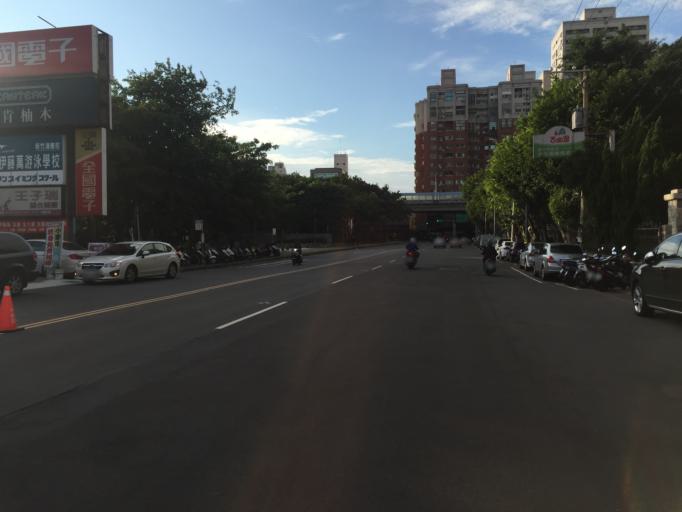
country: TW
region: Taiwan
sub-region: Hsinchu
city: Hsinchu
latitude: 24.8194
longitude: 120.9693
